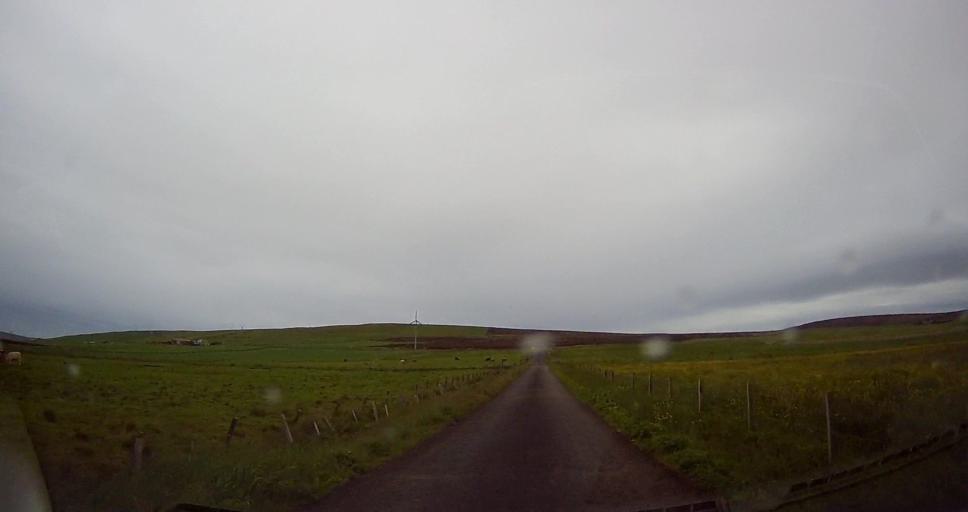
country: GB
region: Scotland
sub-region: Orkney Islands
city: Stromness
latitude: 59.0889
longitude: -3.1829
